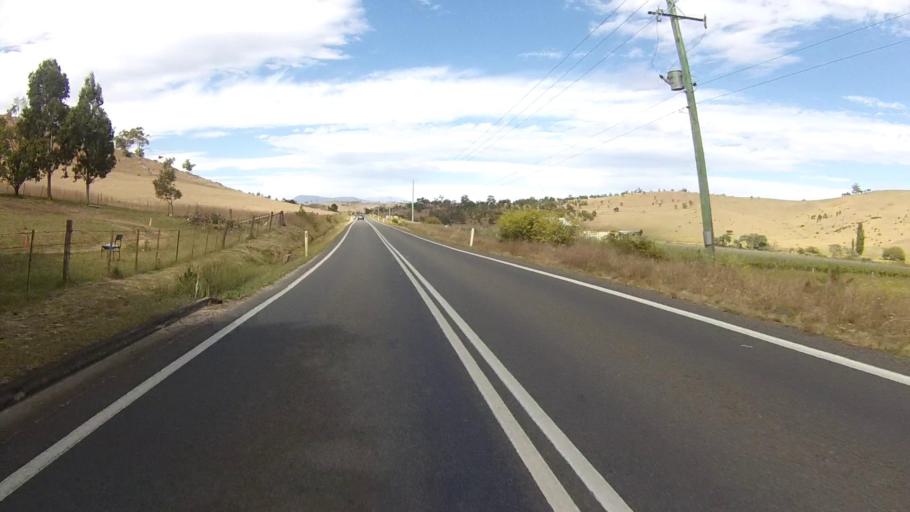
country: AU
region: Tasmania
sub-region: Brighton
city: Old Beach
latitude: -42.6770
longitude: 147.3564
